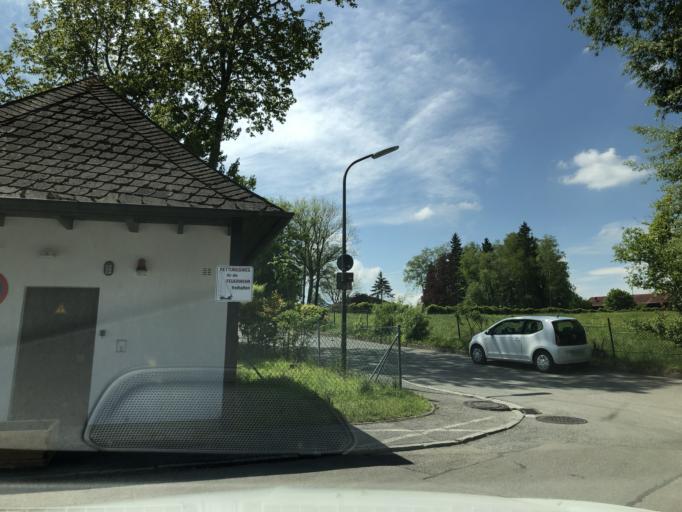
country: DE
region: Bavaria
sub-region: Upper Bavaria
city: Prien am Chiemsee
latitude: 47.8477
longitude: 12.3691
